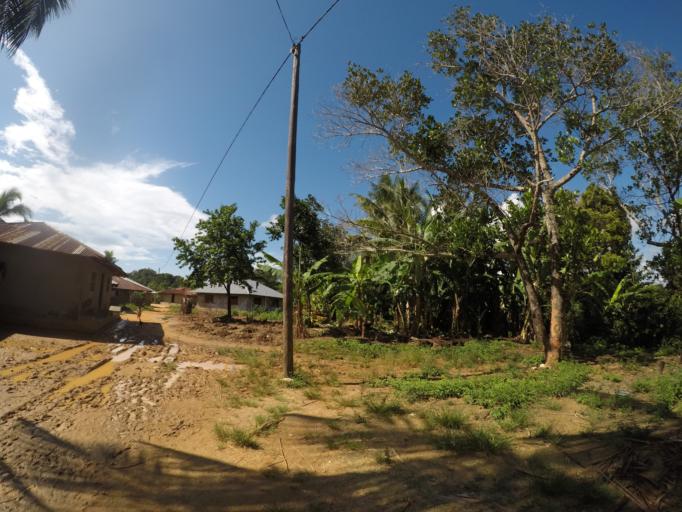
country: TZ
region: Pemba South
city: Mtambile
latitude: -5.3446
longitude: 39.6892
